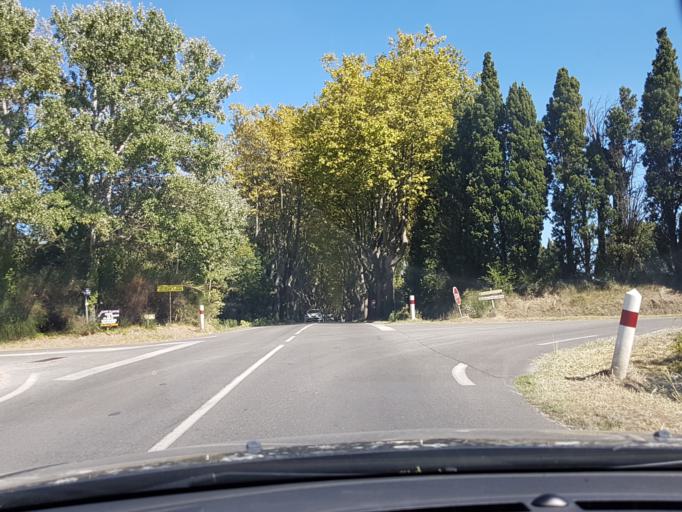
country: FR
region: Provence-Alpes-Cote d'Azur
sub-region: Departement des Bouches-du-Rhone
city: Saint-Remy-de-Provence
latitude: 43.7850
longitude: 4.8702
